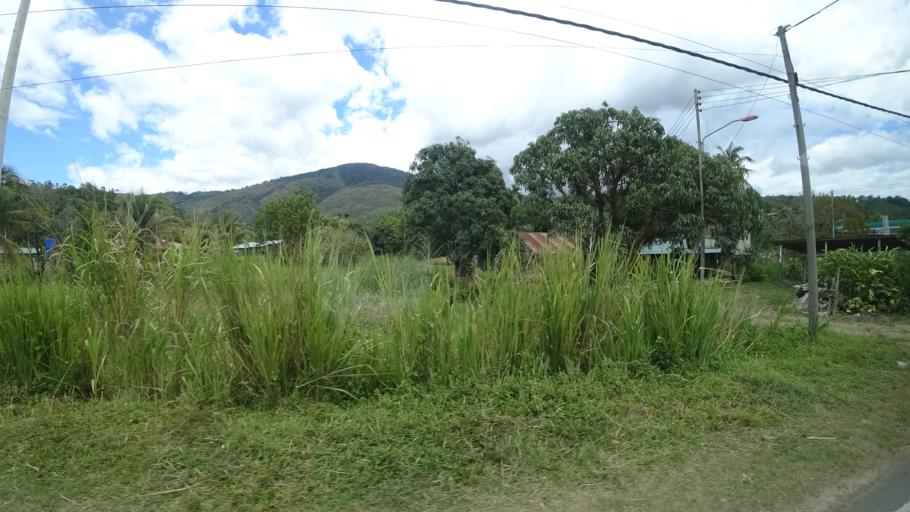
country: MY
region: Sabah
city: Ranau
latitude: 5.9773
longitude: 116.6807
